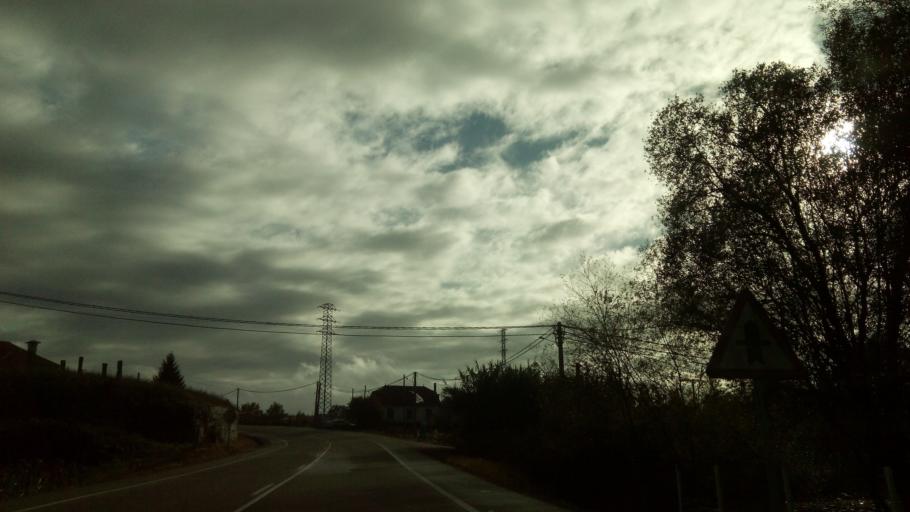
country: ES
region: Galicia
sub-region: Provincia de Pontevedra
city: Ponteareas
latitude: 42.1902
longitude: -8.5084
